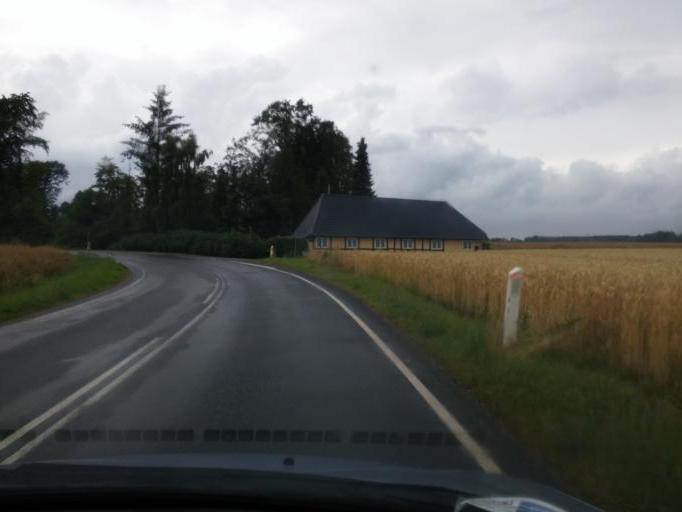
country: DK
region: South Denmark
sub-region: Kerteminde Kommune
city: Langeskov
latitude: 55.4055
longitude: 10.5615
